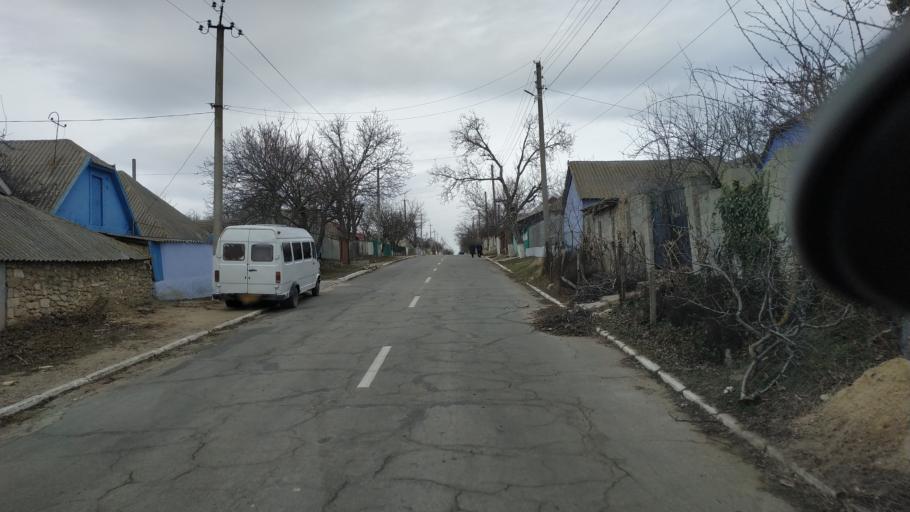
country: MD
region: Telenesti
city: Cocieri
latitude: 47.3453
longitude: 29.1180
